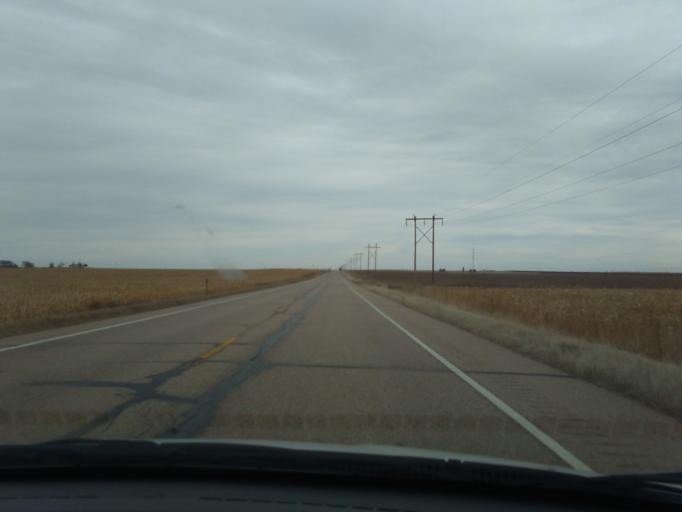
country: US
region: Colorado
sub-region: Yuma County
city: Yuma
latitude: 40.1480
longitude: -102.8412
